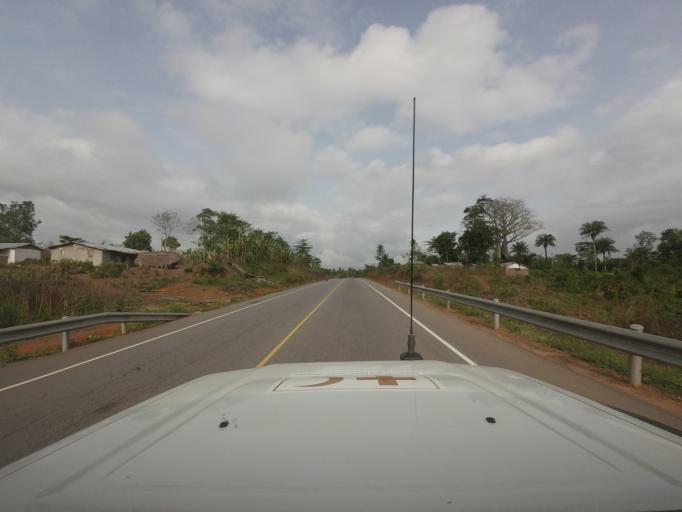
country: LR
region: Bong
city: Gbarnga
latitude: 7.0048
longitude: -9.3022
